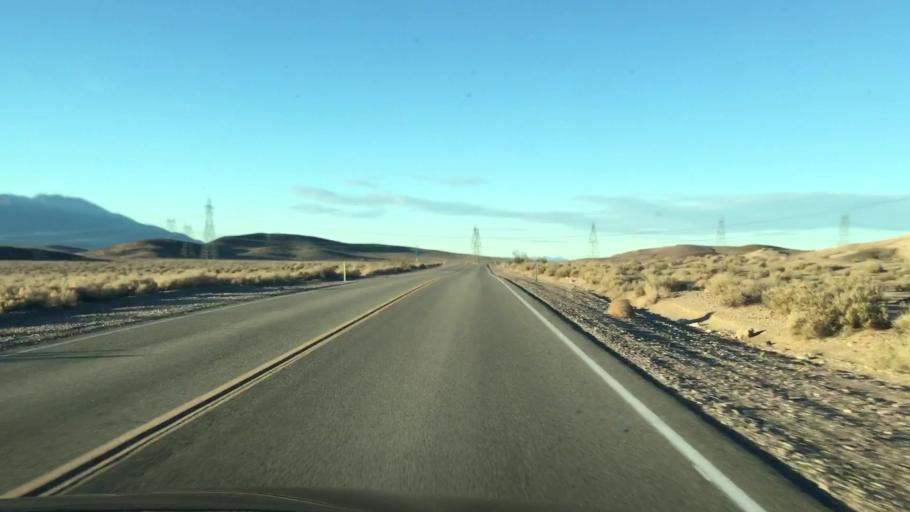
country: US
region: California
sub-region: San Bernardino County
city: Fort Irwin
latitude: 35.3802
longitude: -116.1232
